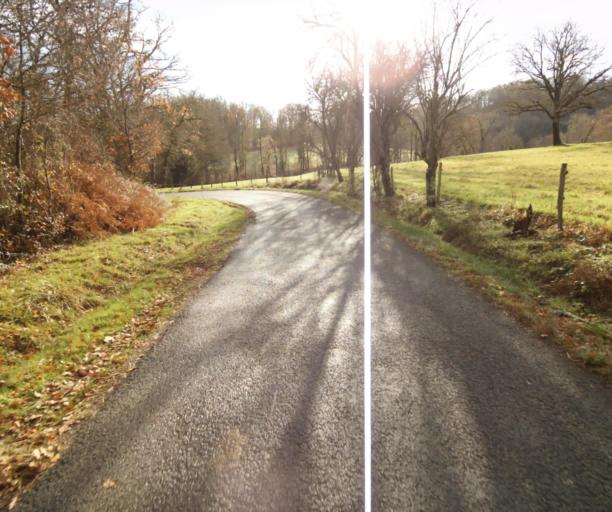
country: FR
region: Limousin
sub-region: Departement de la Correze
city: Sainte-Fereole
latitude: 45.2578
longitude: 1.6024
